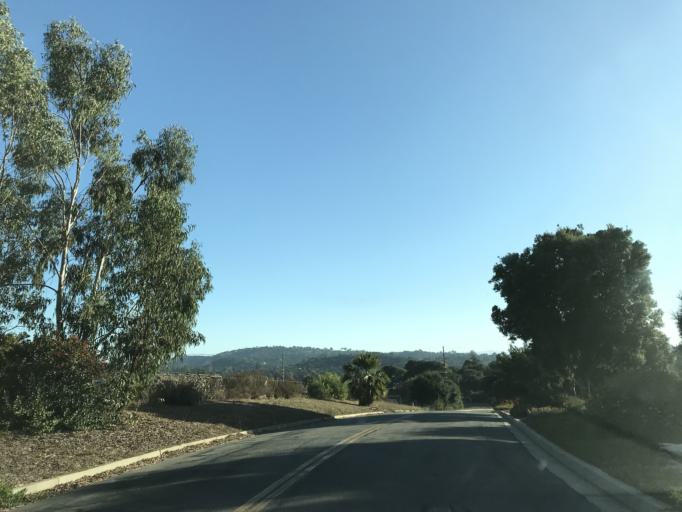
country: US
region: California
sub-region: Santa Barbara County
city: Mission Canyon
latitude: 34.4513
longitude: -119.7687
